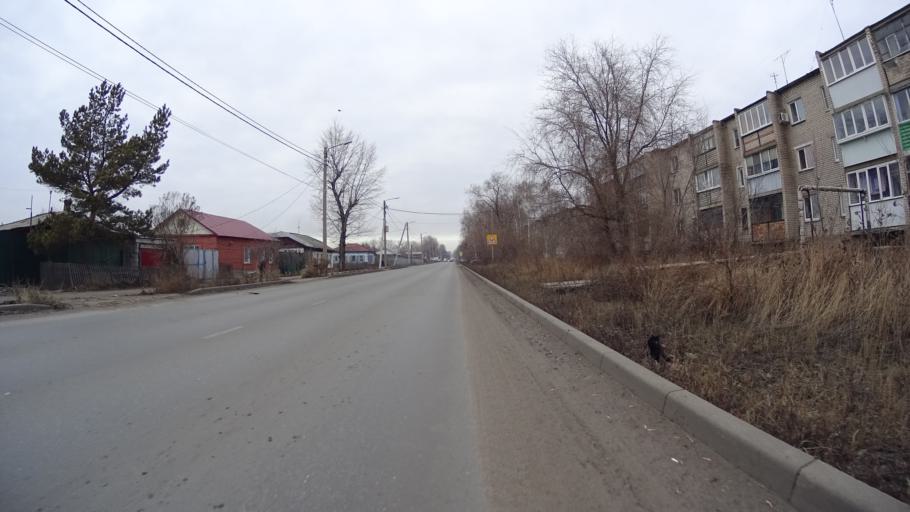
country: RU
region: Chelyabinsk
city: Troitsk
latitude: 54.1086
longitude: 61.5715
